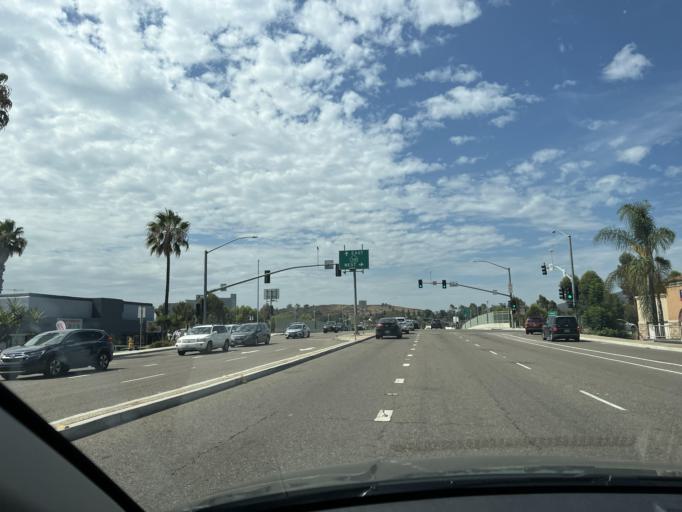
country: US
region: California
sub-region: San Diego County
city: Escondido
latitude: 33.1332
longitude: -117.1208
